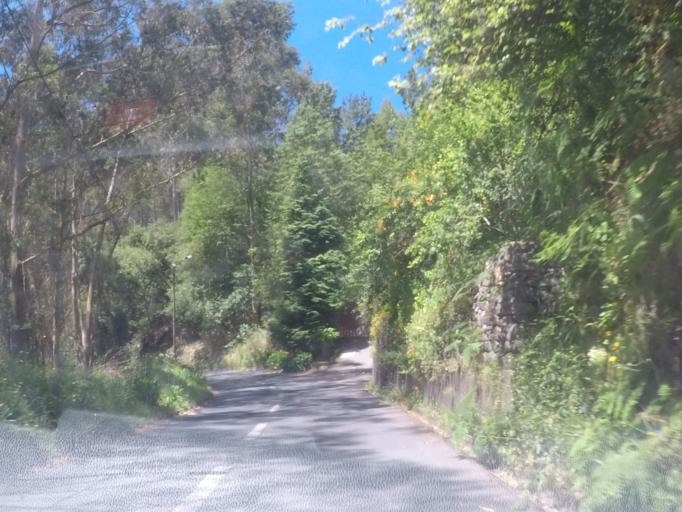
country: PT
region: Madeira
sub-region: Camara de Lobos
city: Curral das Freiras
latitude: 32.6896
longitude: -16.9753
